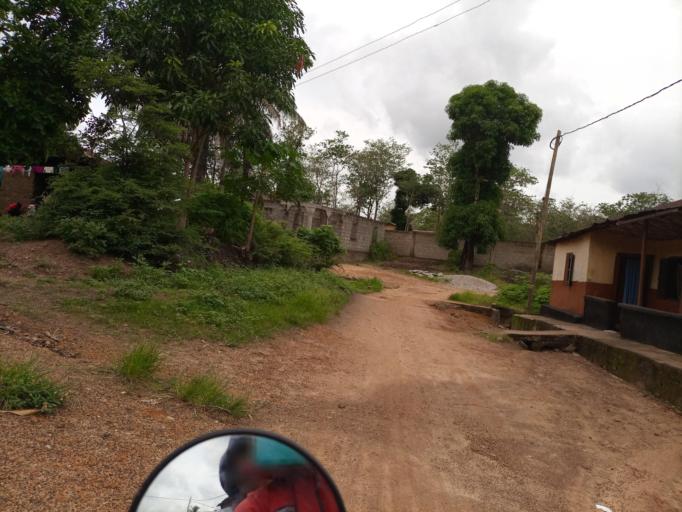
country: SL
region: Southern Province
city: Bo
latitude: 7.9561
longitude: -11.7431
